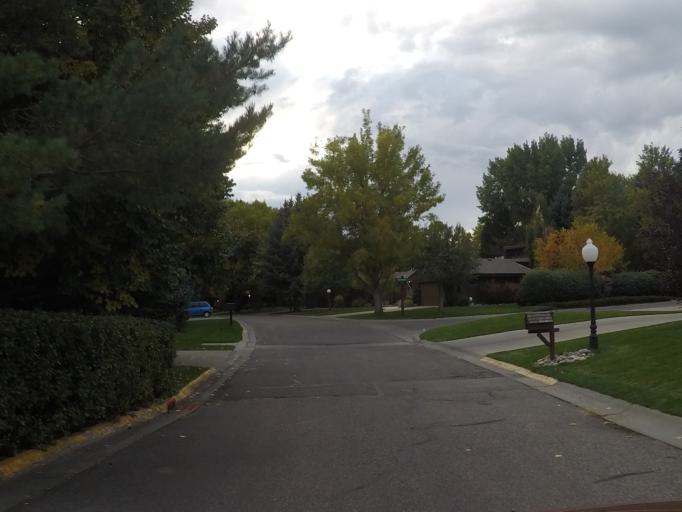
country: US
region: Montana
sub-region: Yellowstone County
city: Billings
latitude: 45.7935
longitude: -108.5513
